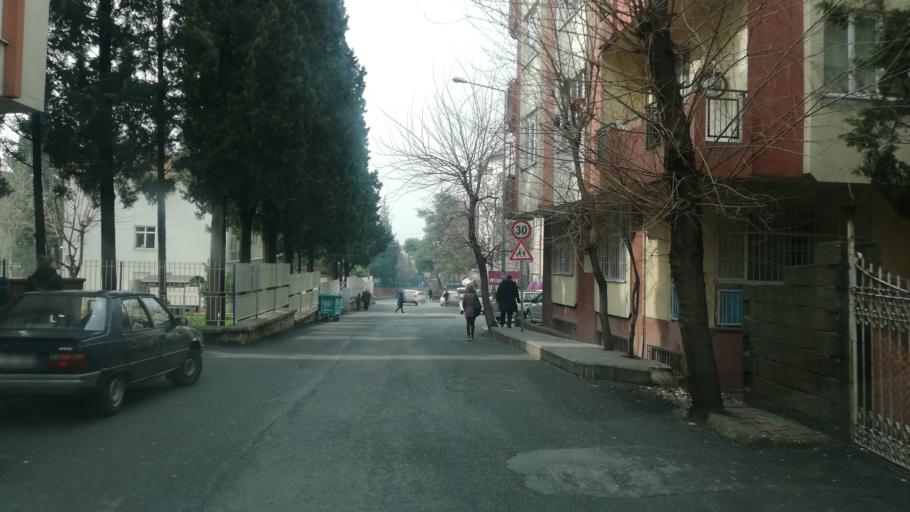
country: TR
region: Kahramanmaras
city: Kahramanmaras
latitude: 37.5738
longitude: 36.9293
